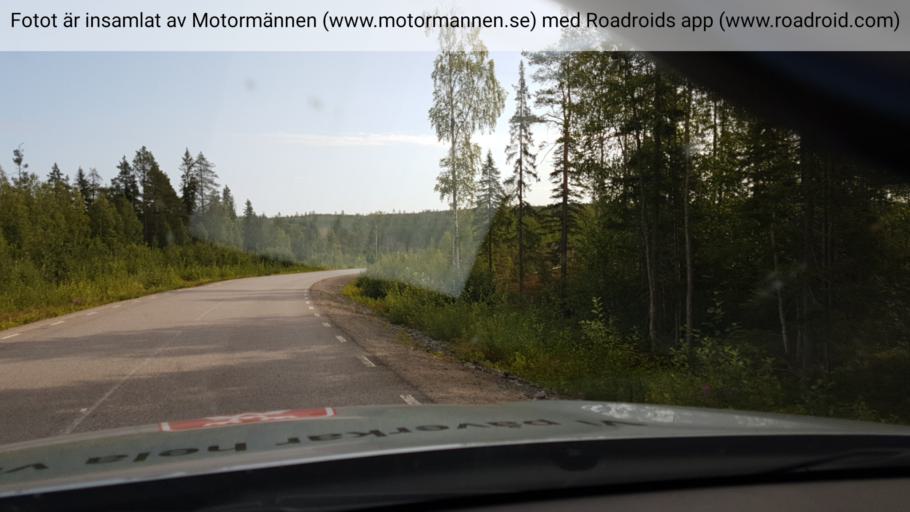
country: SE
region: Norrbotten
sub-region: Alvsbyns Kommun
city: AElvsbyn
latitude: 65.5472
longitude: 20.6159
